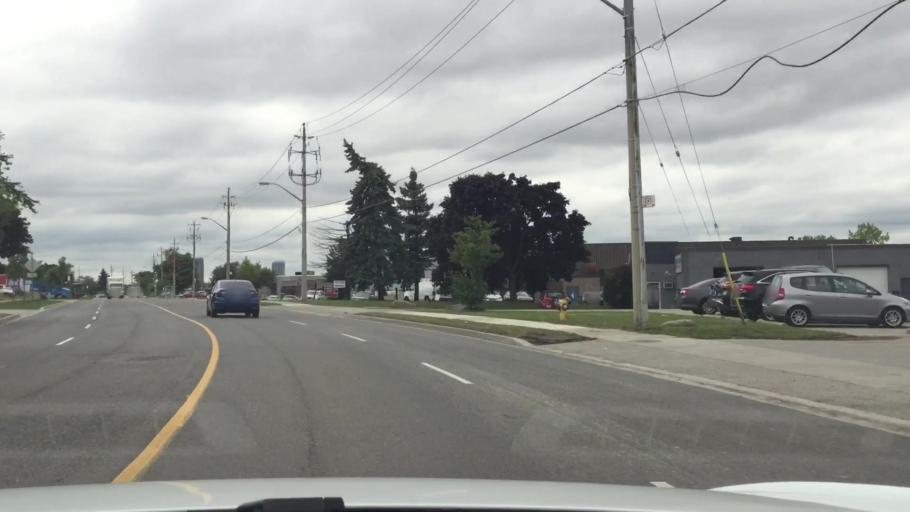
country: CA
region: Ontario
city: Scarborough
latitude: 43.7962
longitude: -79.2516
